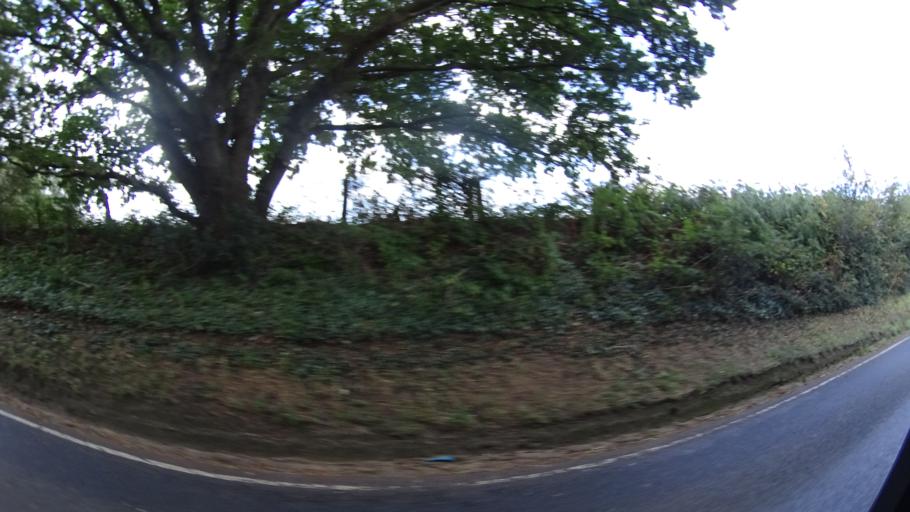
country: GB
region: England
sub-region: Dorset
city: Lytchett Matravers
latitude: 50.7599
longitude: -2.0545
